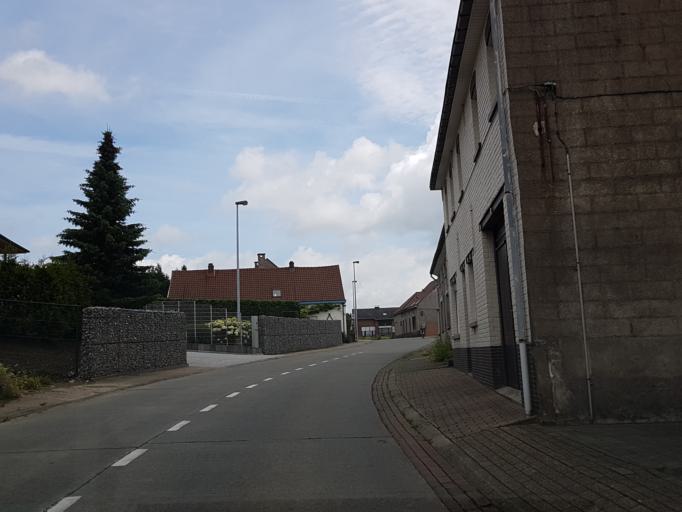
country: BE
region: Flanders
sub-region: Provincie Vlaams-Brabant
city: Ternat
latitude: 50.8946
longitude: 4.1370
